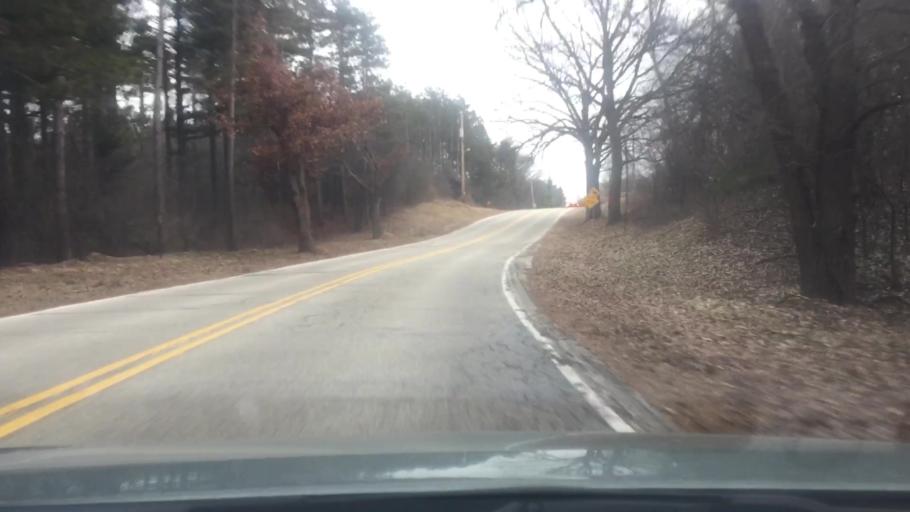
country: US
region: Wisconsin
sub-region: Waukesha County
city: North Prairie
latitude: 42.9427
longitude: -88.4428
